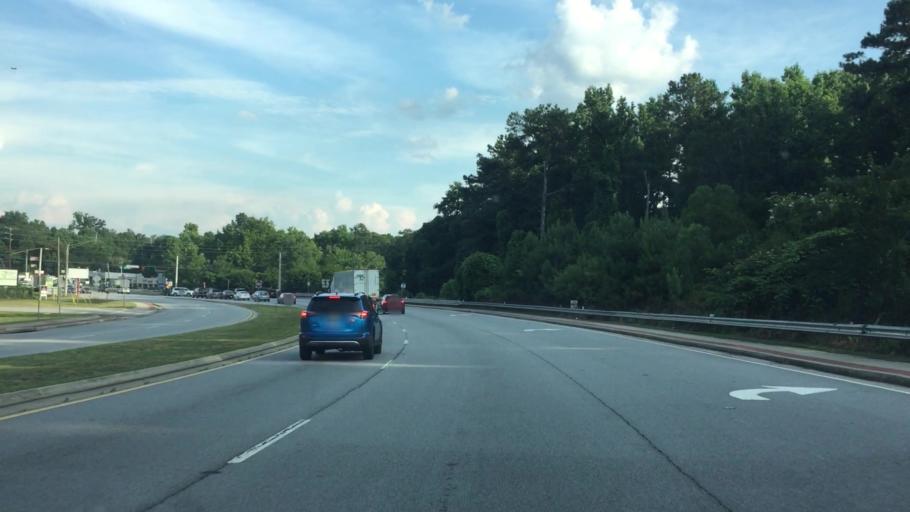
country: US
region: Georgia
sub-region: DeKalb County
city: Panthersville
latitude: 33.6882
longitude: -84.2031
